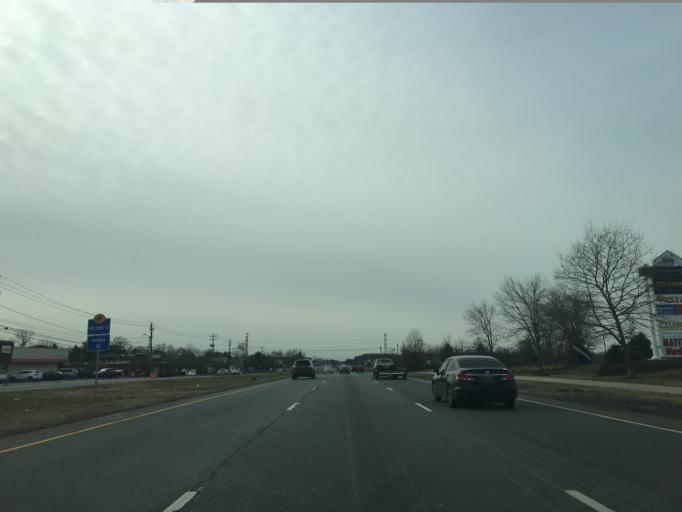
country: US
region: Delaware
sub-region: New Castle County
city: Bear
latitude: 39.6300
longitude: -75.6657
